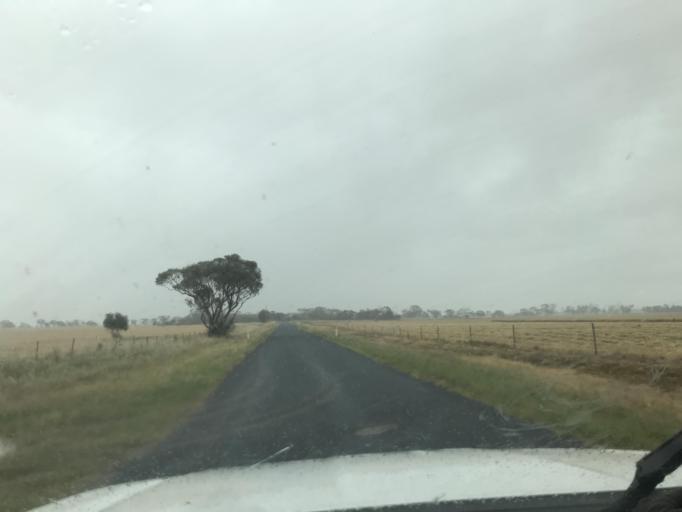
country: AU
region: South Australia
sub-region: Tatiara
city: Bordertown
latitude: -36.3190
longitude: 141.1921
